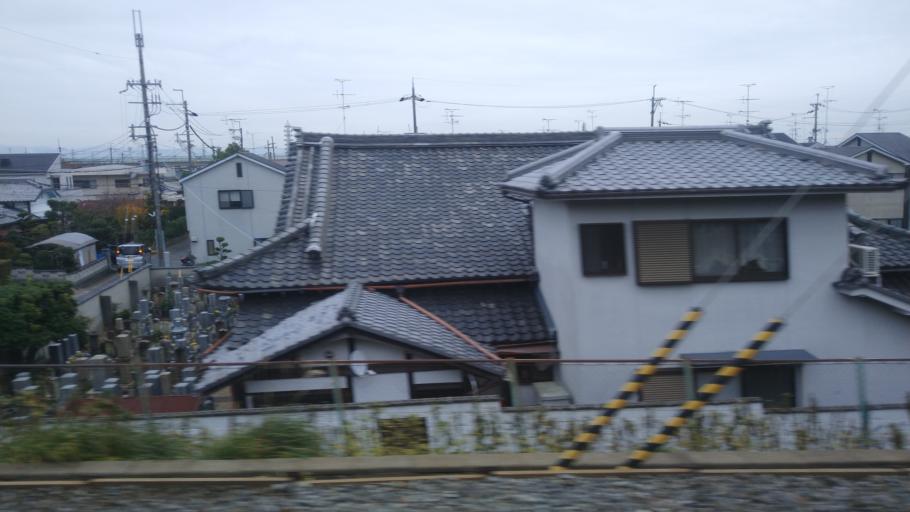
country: JP
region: Kyoto
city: Yawata
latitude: 34.9055
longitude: 135.6865
